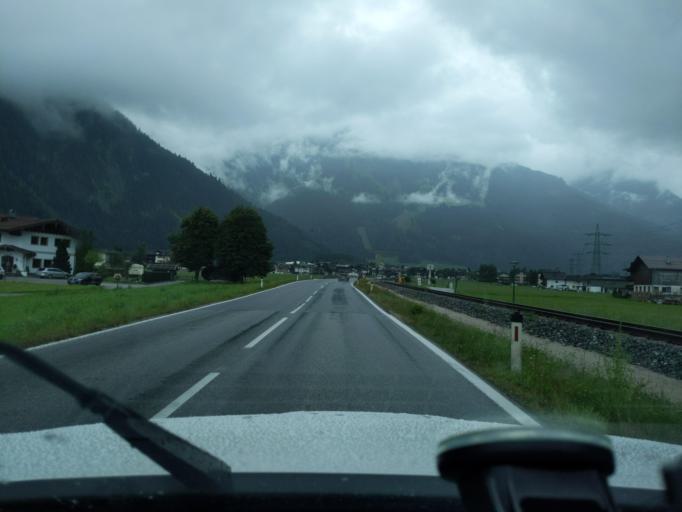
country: AT
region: Tyrol
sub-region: Politischer Bezirk Schwaz
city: Mayrhofen
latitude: 47.1767
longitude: 11.8656
